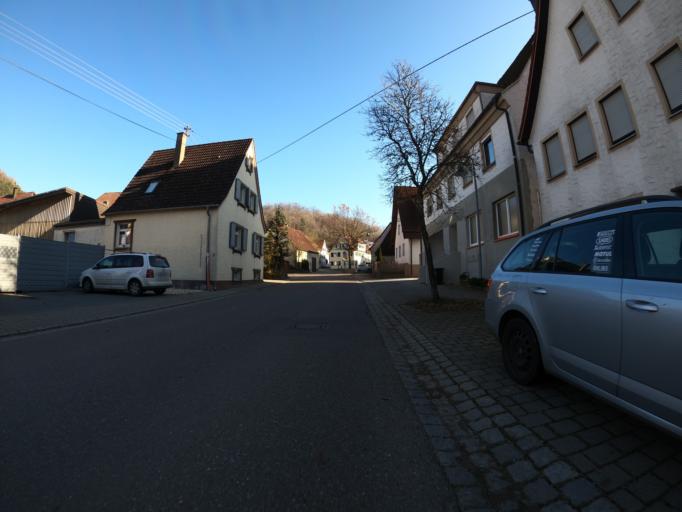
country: DE
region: Baden-Wuerttemberg
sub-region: Regierungsbezirk Stuttgart
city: Bad Ditzenbach
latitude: 48.6165
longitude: 9.6805
